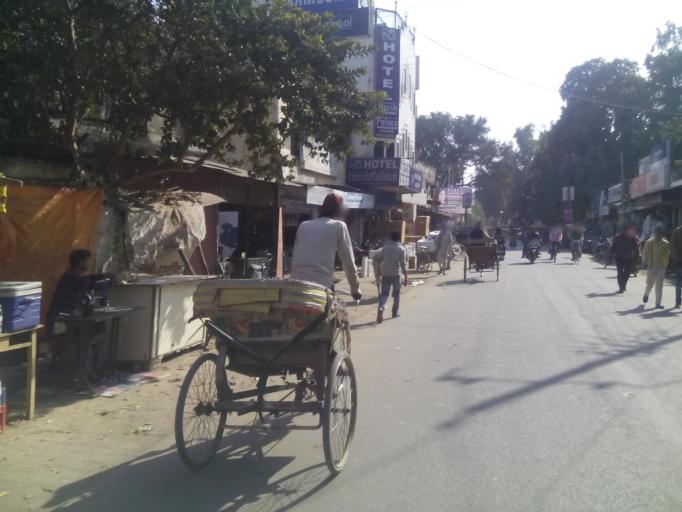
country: IN
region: Uttar Pradesh
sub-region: Bahraich
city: Bahraich
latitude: 27.5709
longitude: 81.5921
